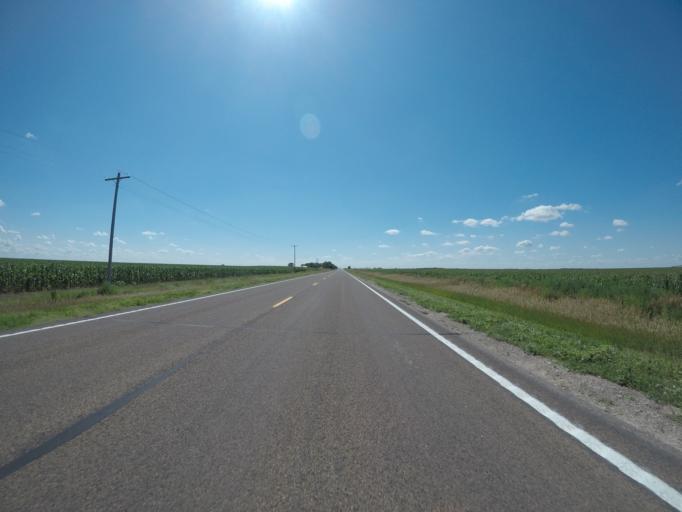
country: US
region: Nebraska
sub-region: Chase County
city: Imperial
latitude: 40.5376
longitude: -101.7247
